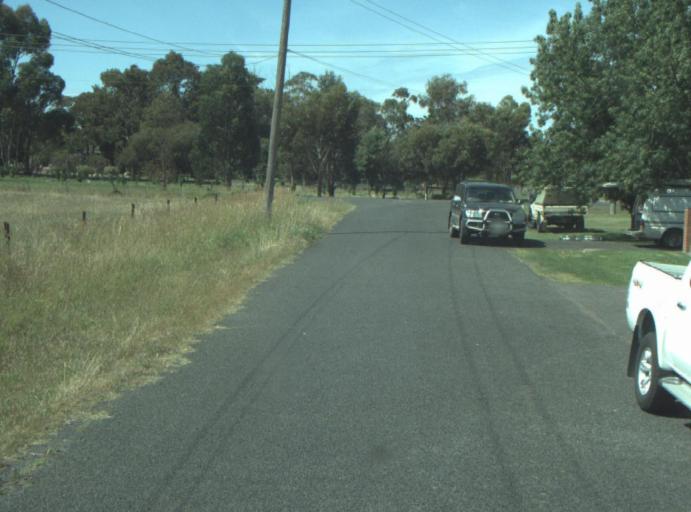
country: AU
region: Victoria
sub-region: Greater Geelong
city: East Geelong
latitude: -38.1719
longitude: 144.4179
